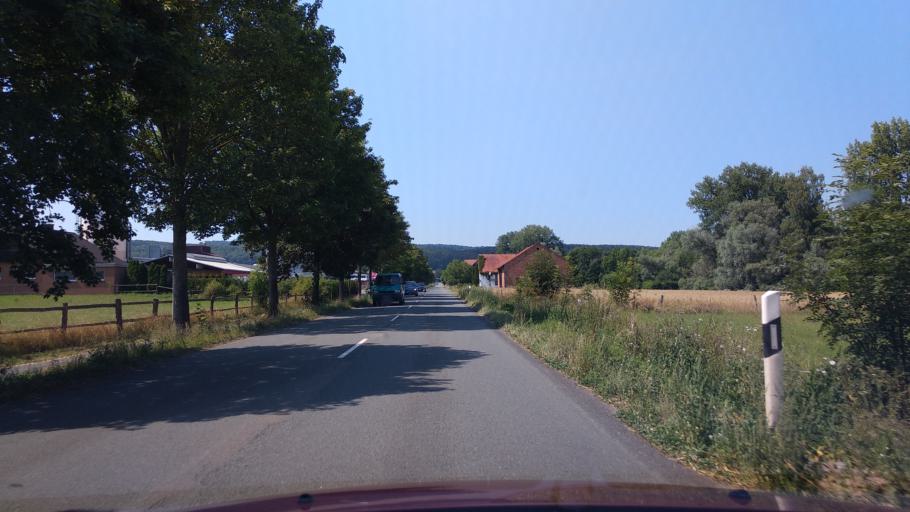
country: DE
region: North Rhine-Westphalia
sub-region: Regierungsbezirk Detmold
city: Bad Driburg
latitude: 51.7111
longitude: 9.0871
